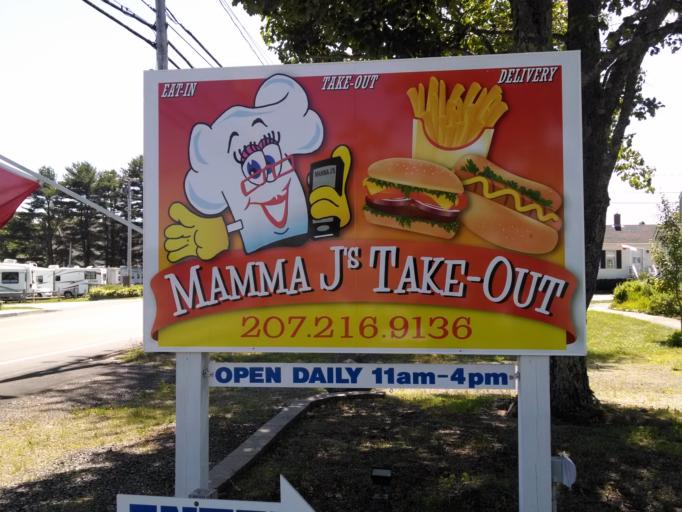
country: US
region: Maine
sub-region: York County
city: Wells Beach Station
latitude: 43.3275
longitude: -70.5769
